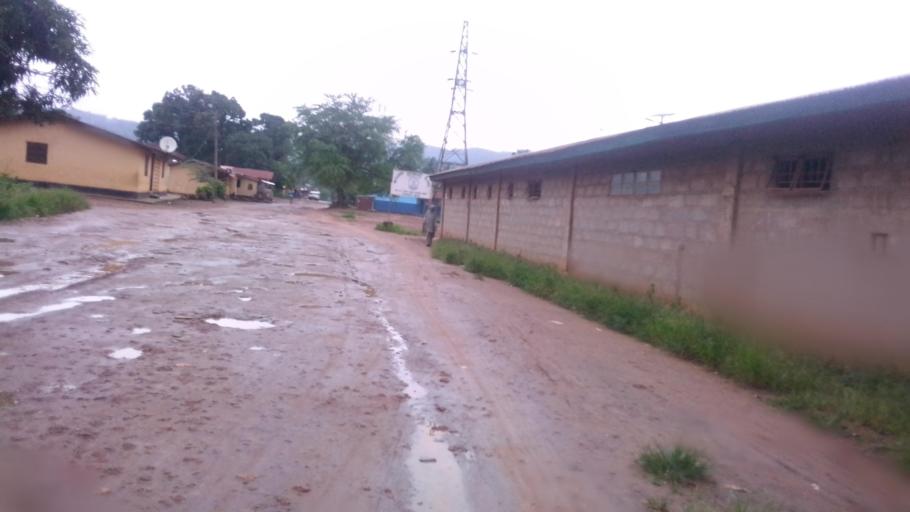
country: SL
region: Eastern Province
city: Kenema
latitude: 7.8867
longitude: -11.1814
